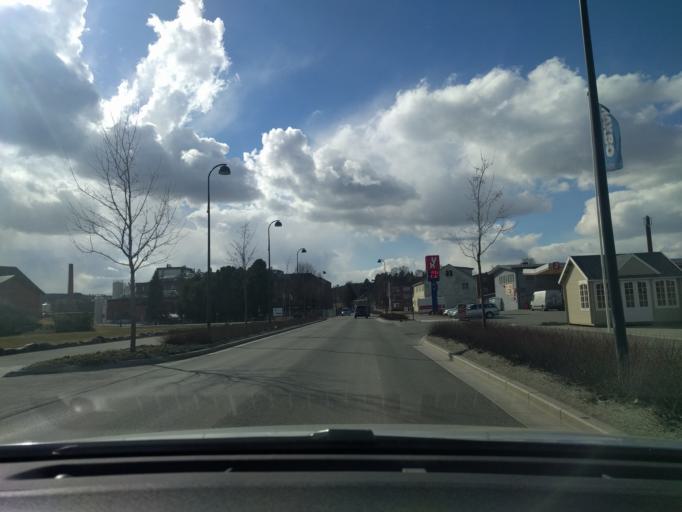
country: NO
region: Hedmark
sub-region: Ringsaker
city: Brumunddal
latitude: 60.8865
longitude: 10.9342
